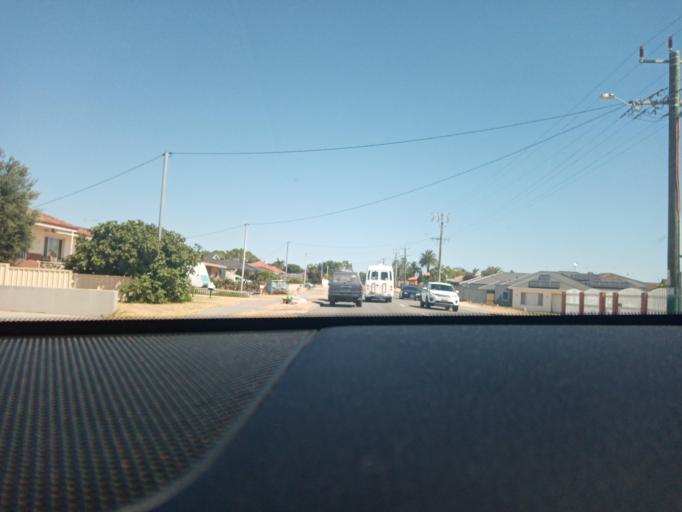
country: AU
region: Western Australia
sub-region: City of Cockburn
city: Coogee
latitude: -32.1255
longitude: 115.7852
